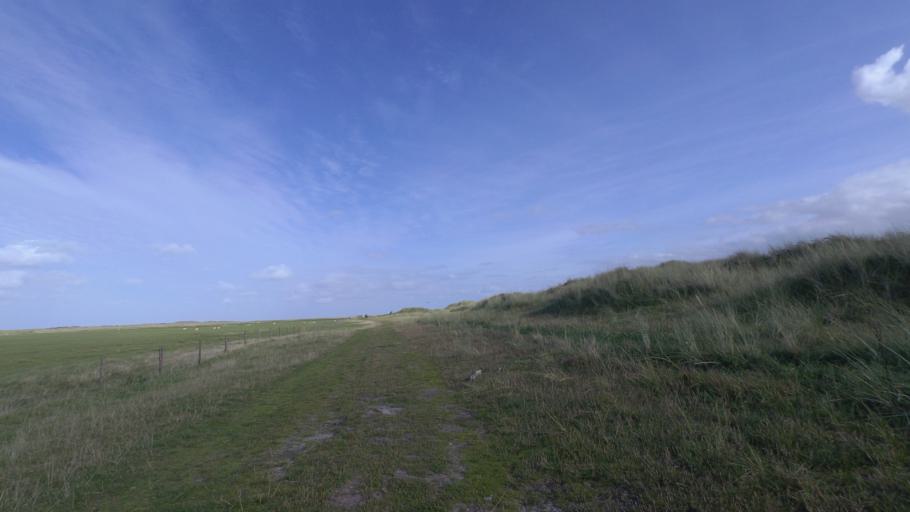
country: NL
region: Friesland
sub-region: Gemeente Ameland
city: Nes
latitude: 53.4509
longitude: 5.8569
